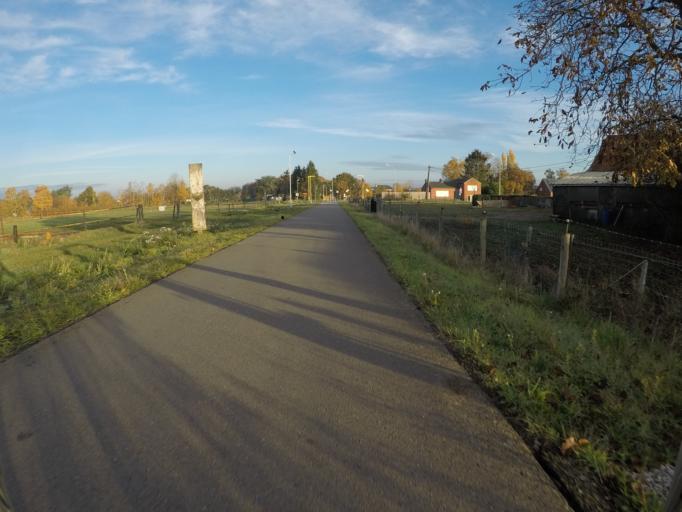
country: BE
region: Flanders
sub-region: Provincie Antwerpen
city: Herentals
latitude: 51.1506
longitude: 4.8209
